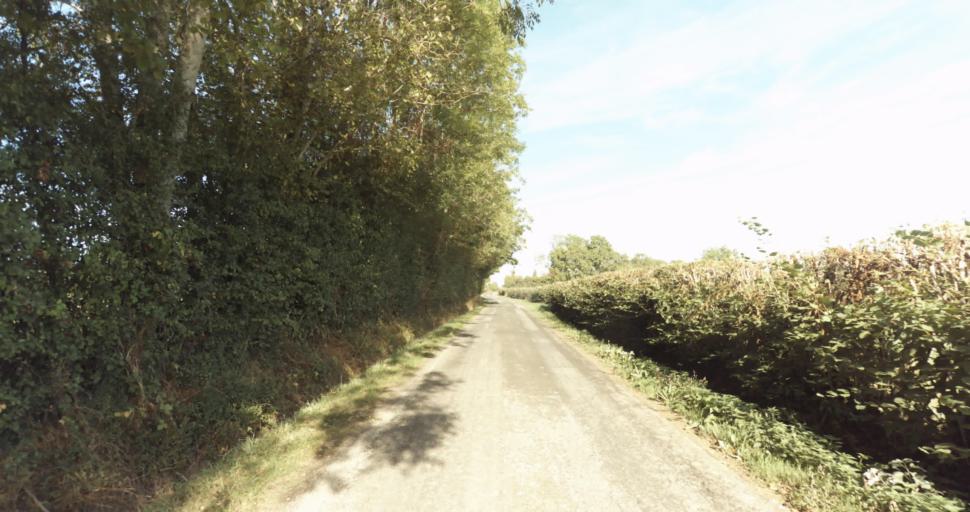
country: FR
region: Lower Normandy
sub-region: Departement de l'Orne
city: Vimoutiers
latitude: 48.9163
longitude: 0.3021
